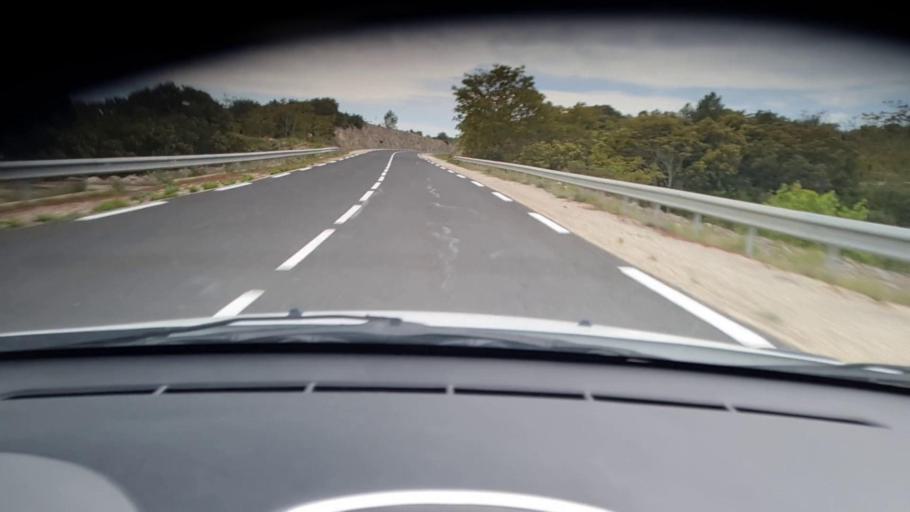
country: FR
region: Languedoc-Roussillon
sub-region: Departement du Gard
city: Poulx
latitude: 43.8916
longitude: 4.3866
